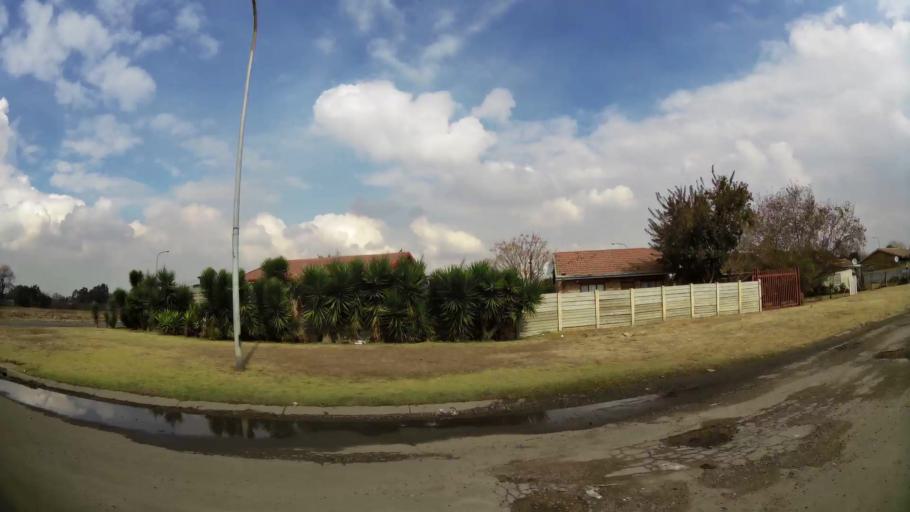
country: ZA
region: Gauteng
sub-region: Sedibeng District Municipality
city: Vereeniging
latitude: -26.6663
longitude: 27.9158
